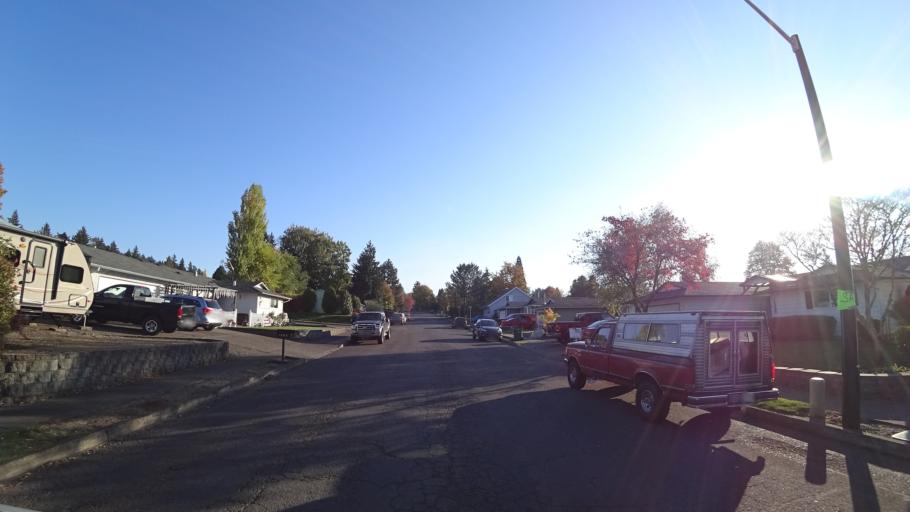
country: US
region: Oregon
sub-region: Multnomah County
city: Gresham
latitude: 45.4857
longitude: -122.4552
